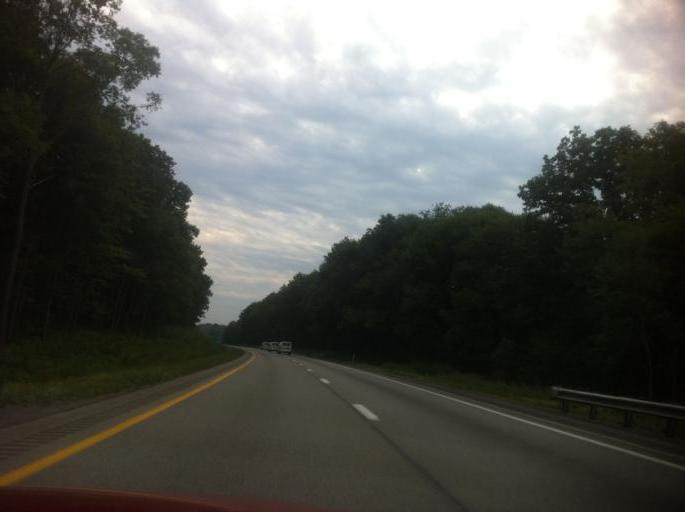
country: US
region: Pennsylvania
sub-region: Mercer County
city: Grove City
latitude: 41.2047
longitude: -79.9272
